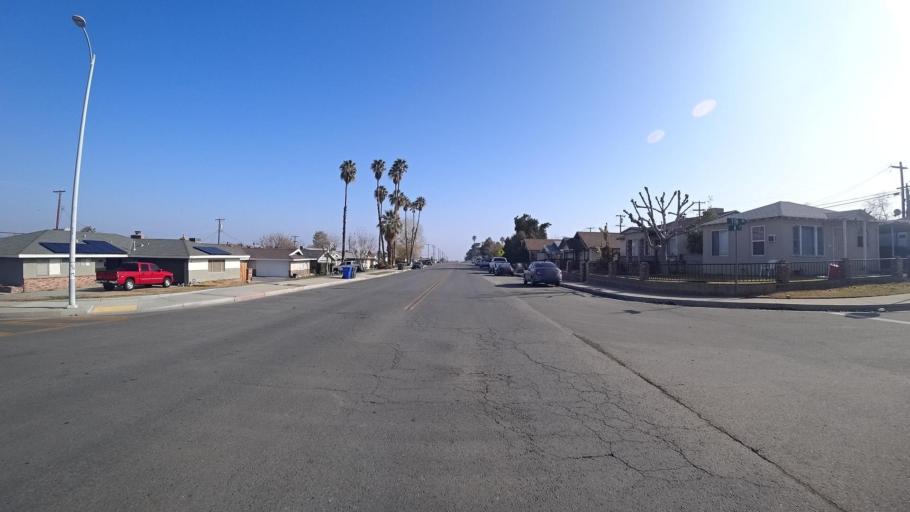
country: US
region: California
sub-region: Kern County
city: Taft Heights
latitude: 35.1367
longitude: -119.4711
